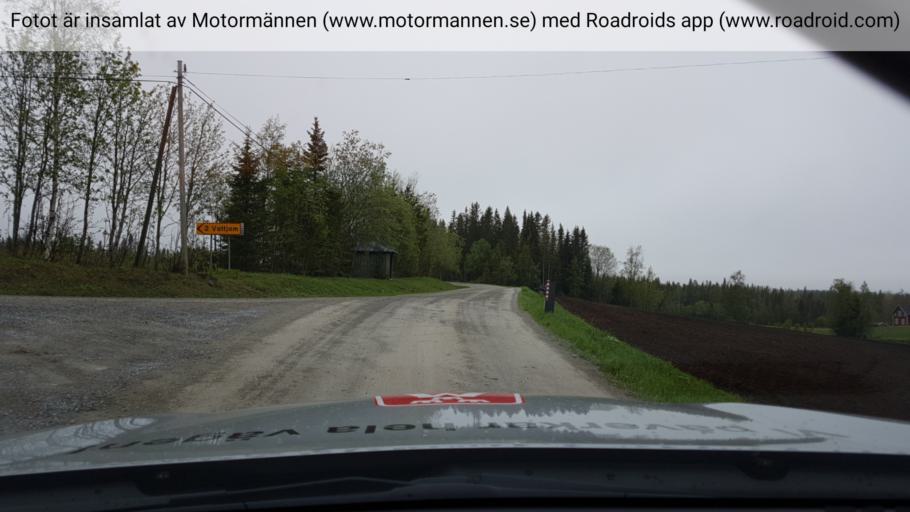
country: SE
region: Jaemtland
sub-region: Bergs Kommun
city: Hoverberg
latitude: 63.0168
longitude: 14.3824
